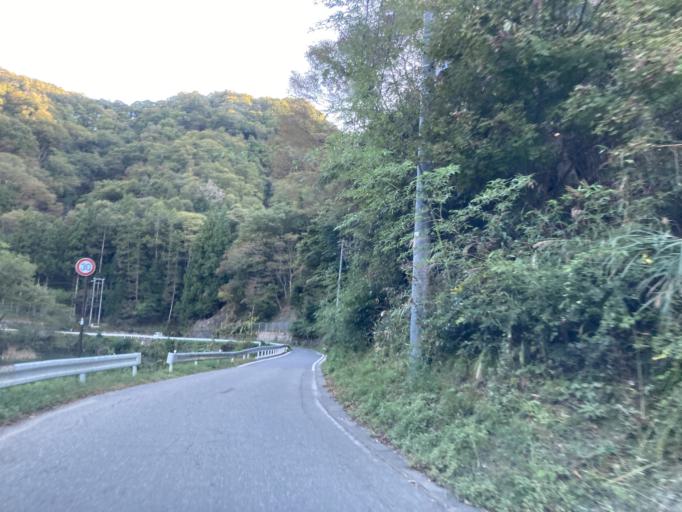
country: JP
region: Nagano
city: Omachi
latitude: 36.4610
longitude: 137.9605
